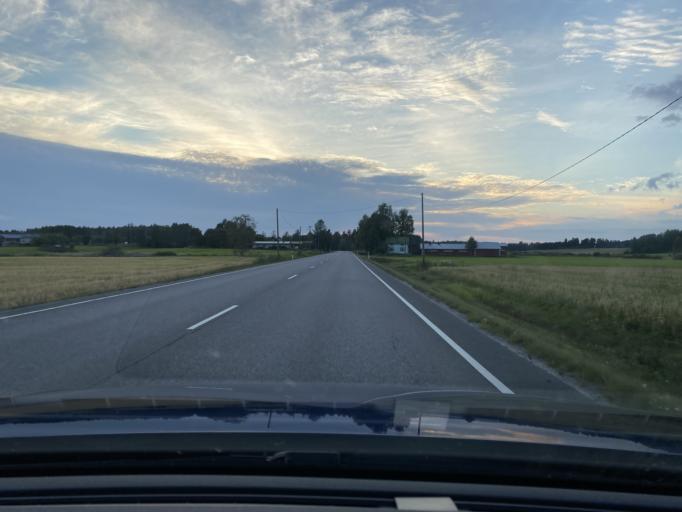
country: FI
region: Satakunta
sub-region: Pohjois-Satakunta
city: Kankaanpaeae
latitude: 61.7630
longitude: 22.4949
